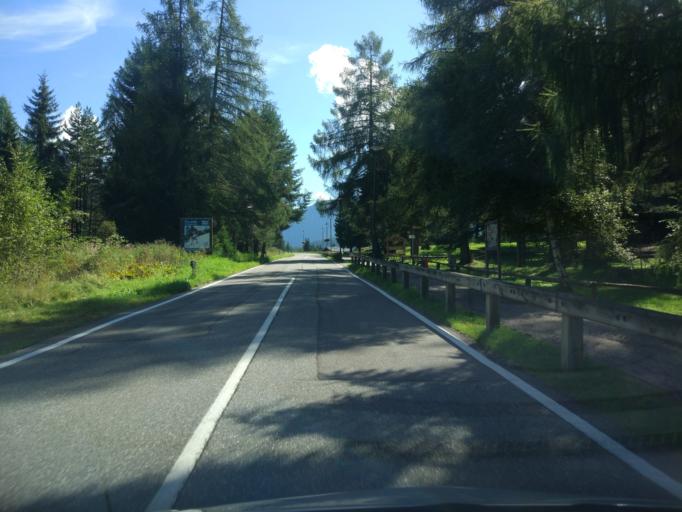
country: IT
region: Trentino-Alto Adige
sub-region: Provincia di Trento
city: Moena
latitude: 46.3114
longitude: 11.6712
